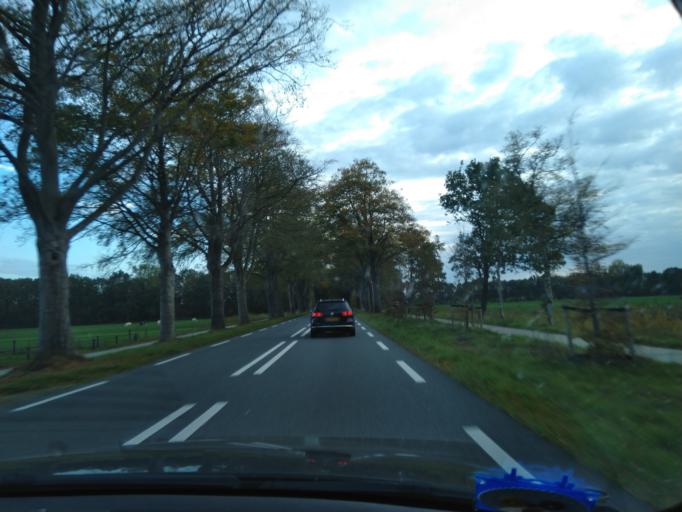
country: NL
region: Drenthe
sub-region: Gemeente Tynaarlo
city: Vries
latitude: 53.0616
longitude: 6.5764
